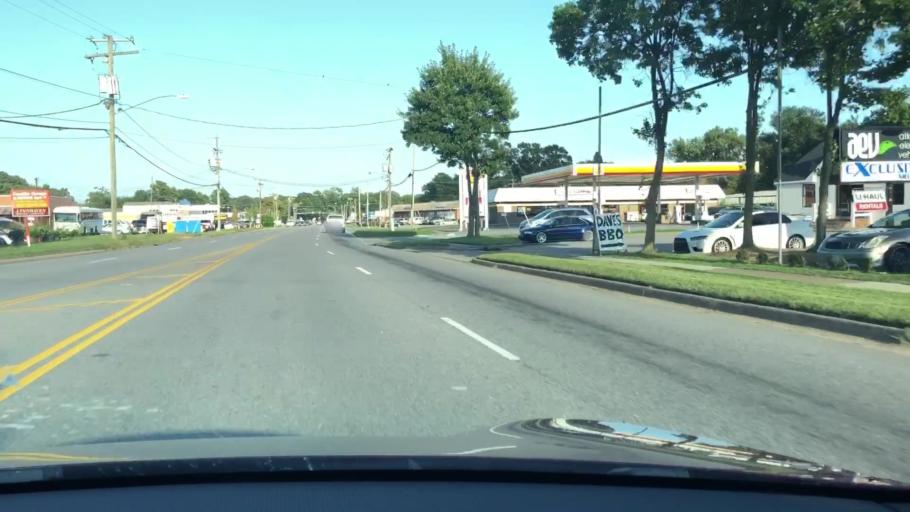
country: US
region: Virginia
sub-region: City of Virginia Beach
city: Virginia Beach
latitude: 36.8432
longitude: -76.0271
